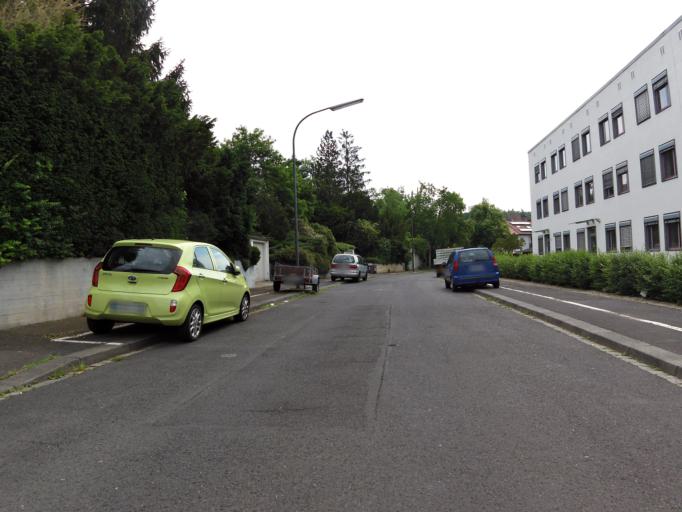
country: DE
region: Bavaria
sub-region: Regierungsbezirk Unterfranken
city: Wuerzburg
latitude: 49.7870
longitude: 9.9560
